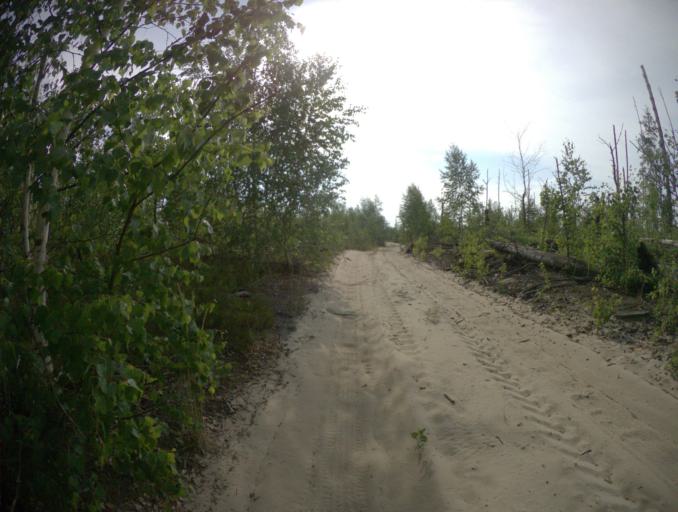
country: RU
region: Ivanovo
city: Talitsy
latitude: 56.4299
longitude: 42.3111
